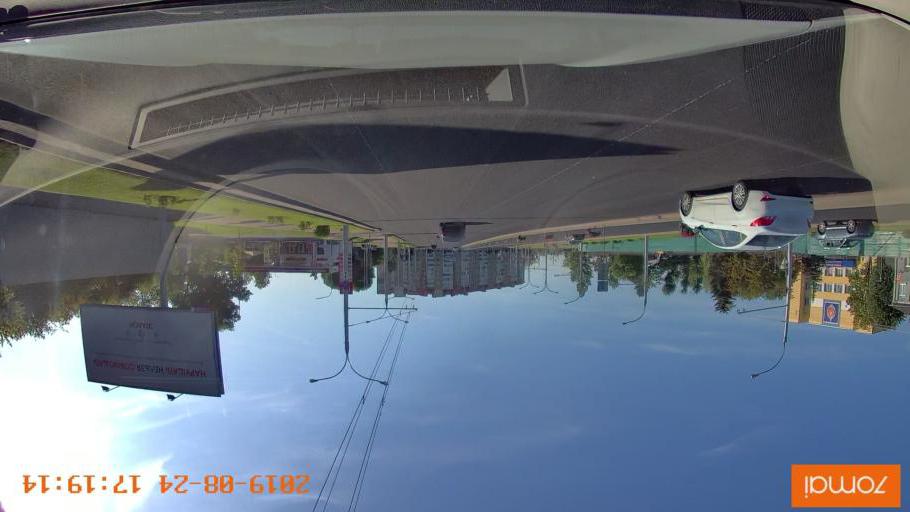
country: BY
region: Minsk
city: Vyaliki Trastsyanets
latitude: 53.8634
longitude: 27.6422
